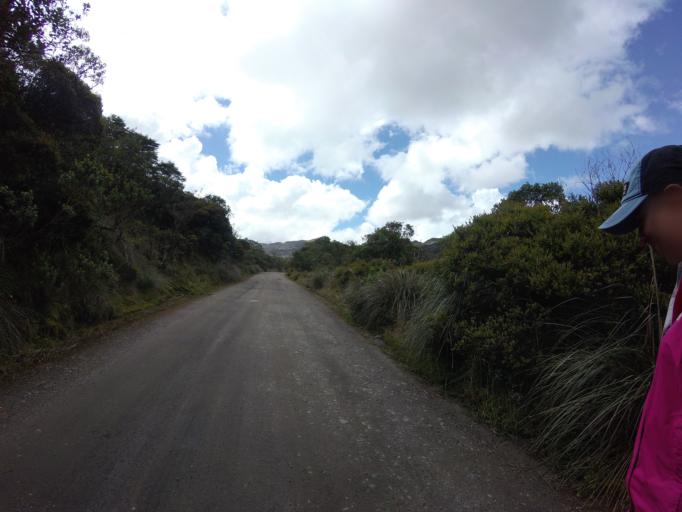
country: CO
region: Cundinamarca
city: Junin
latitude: 4.6248
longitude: -73.7227
